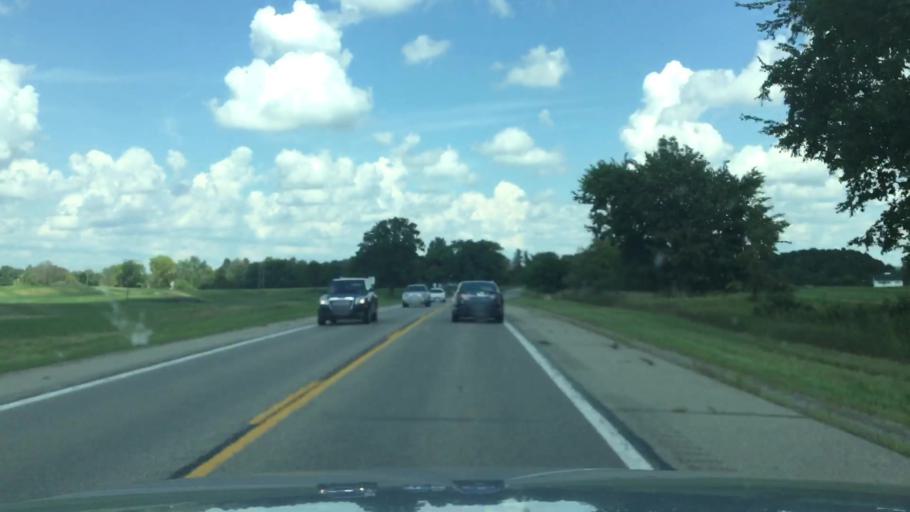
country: US
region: Michigan
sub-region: Lenawee County
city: Clinton
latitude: 42.1042
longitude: -83.8966
